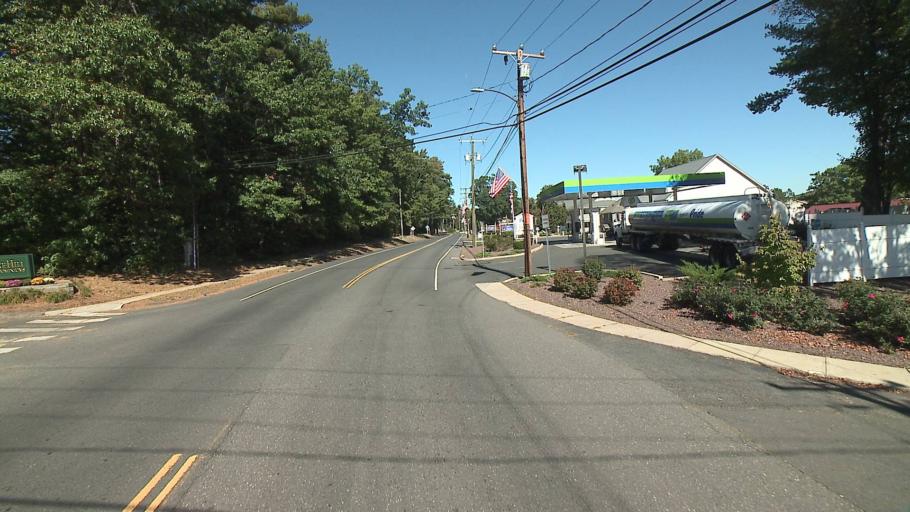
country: US
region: Connecticut
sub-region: Hartford County
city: Simsbury Center
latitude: 41.8595
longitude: -72.8108
